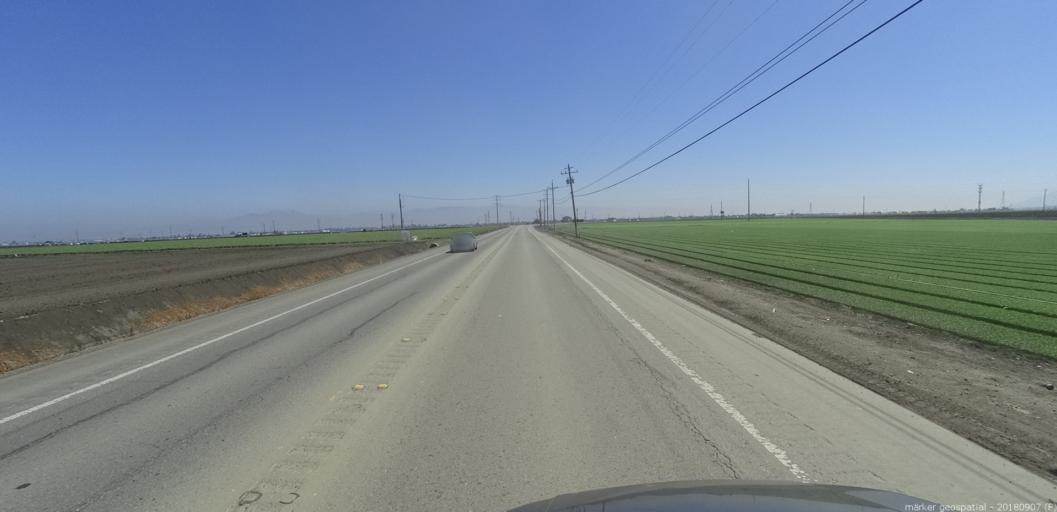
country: US
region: California
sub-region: Monterey County
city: Boronda
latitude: 36.6787
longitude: -121.7122
